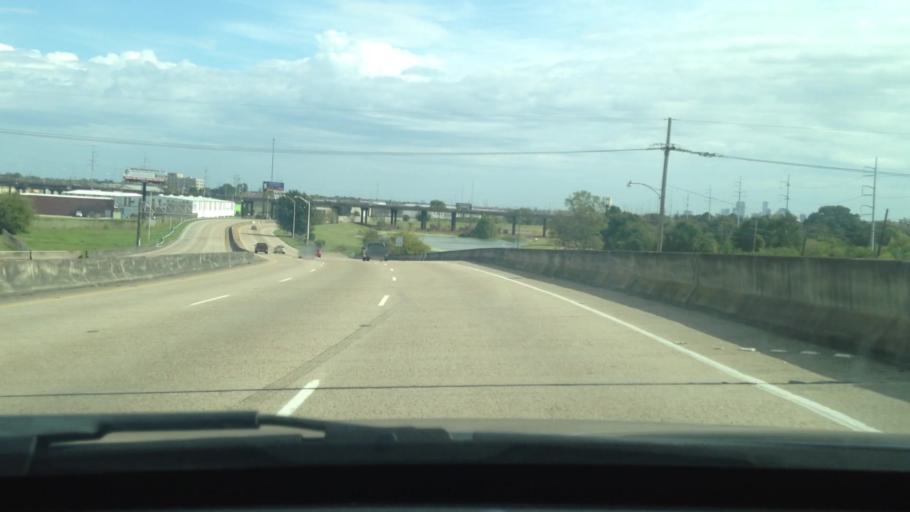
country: US
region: Louisiana
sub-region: Jefferson Parish
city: Metairie Terrace
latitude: 29.9708
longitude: -90.1616
